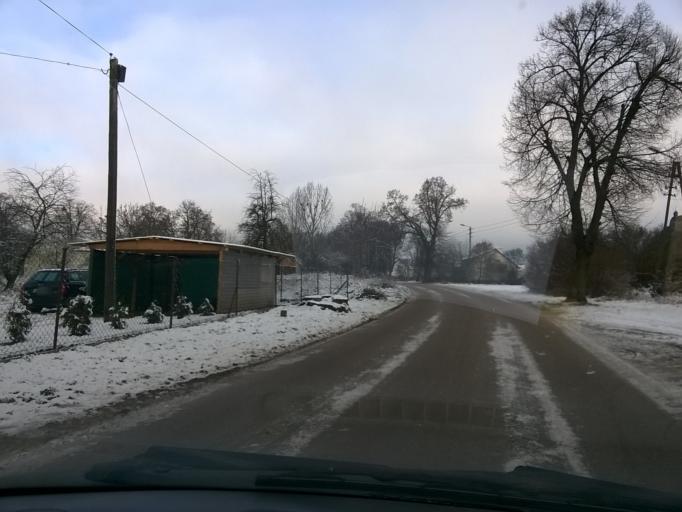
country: PL
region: Kujawsko-Pomorskie
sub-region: Powiat nakielski
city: Kcynia
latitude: 53.0248
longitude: 17.4235
